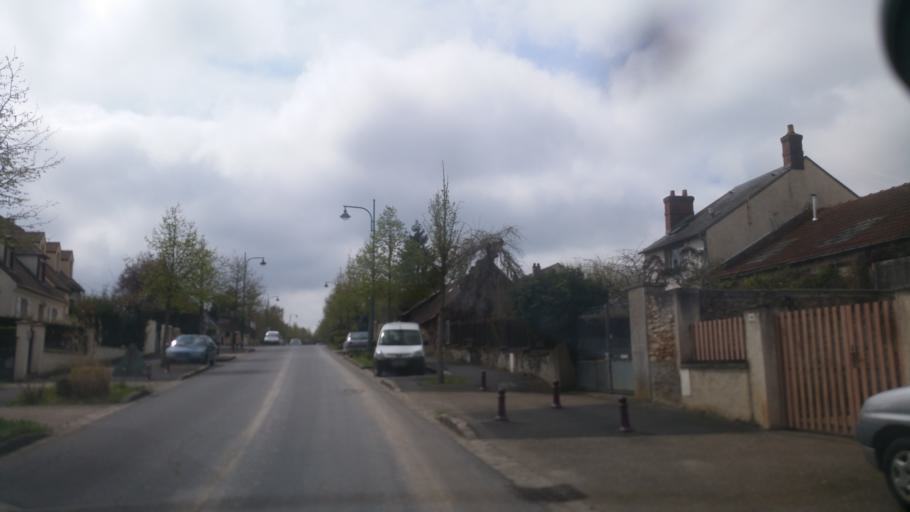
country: FR
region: Ile-de-France
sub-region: Departement de l'Essonne
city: Dourdan
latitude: 48.5265
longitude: 2.0060
